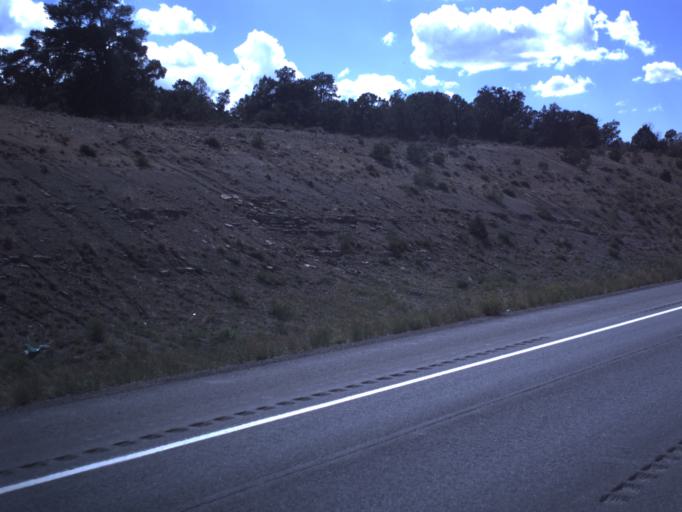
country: US
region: Utah
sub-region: Duchesne County
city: Duchesne
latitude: 40.1829
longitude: -110.6597
